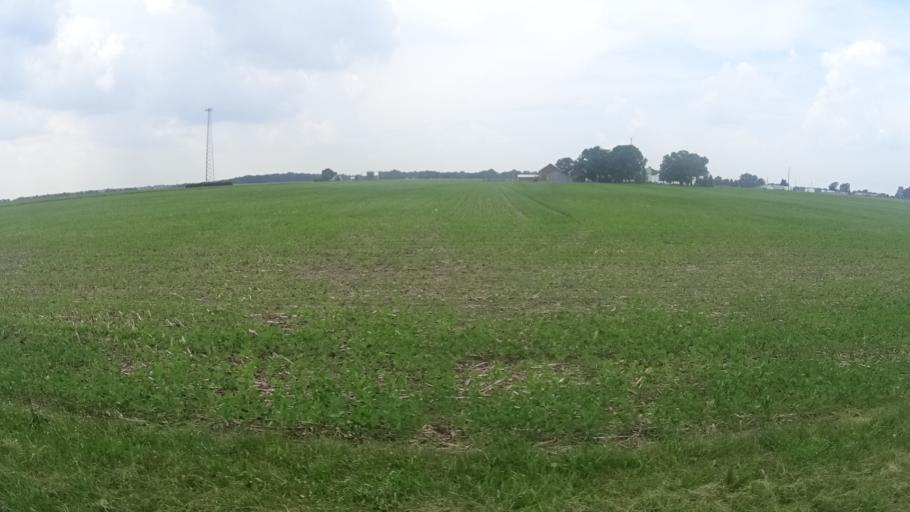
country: US
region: Ohio
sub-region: Huron County
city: Monroeville
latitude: 41.3094
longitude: -82.6852
